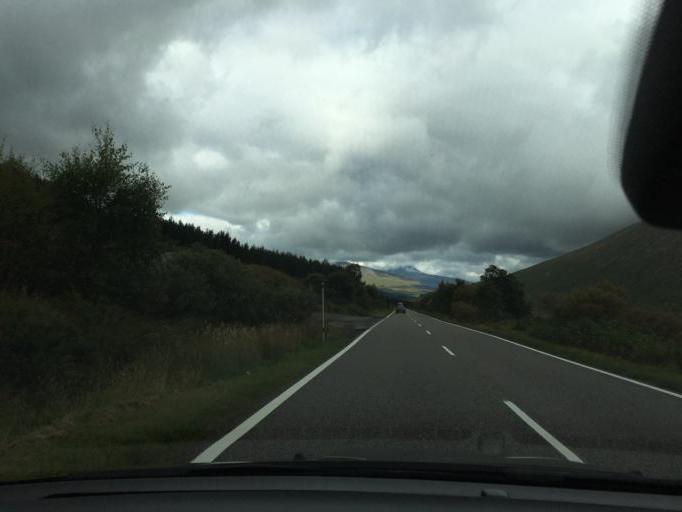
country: GB
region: Scotland
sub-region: Argyll and Bute
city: Garelochhead
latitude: 56.4749
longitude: -4.7288
